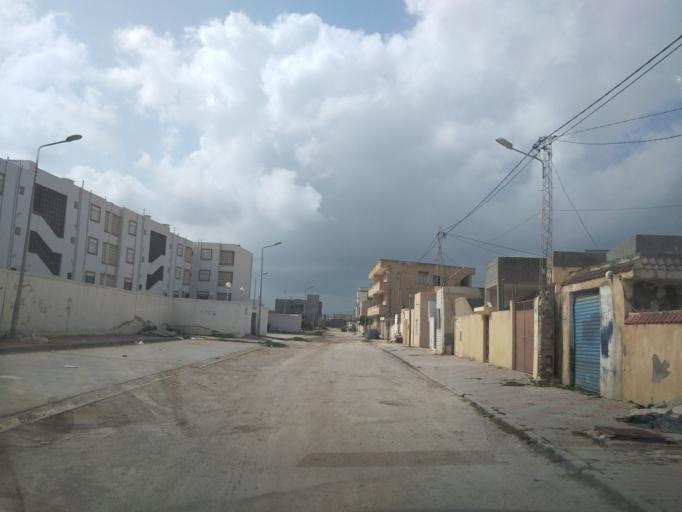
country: TN
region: Ariana
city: Ariana
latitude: 36.9470
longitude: 10.1736
